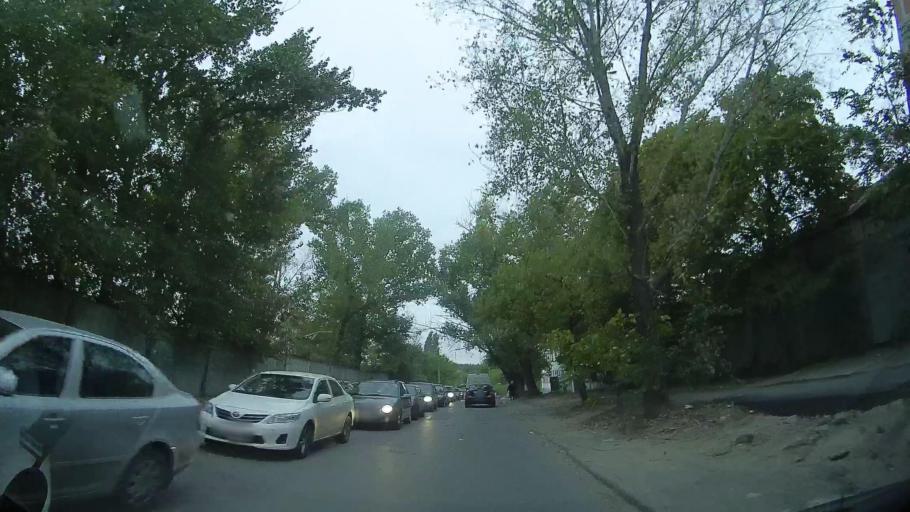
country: RU
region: Rostov
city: Severnyy
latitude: 47.2686
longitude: 39.6832
